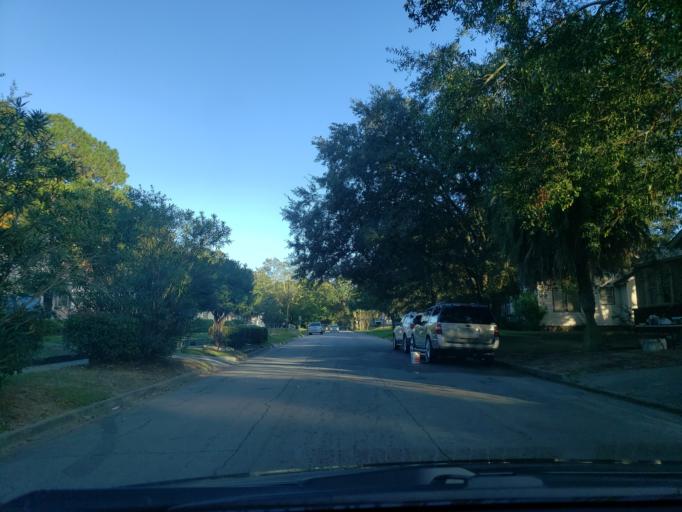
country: US
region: Georgia
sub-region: Chatham County
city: Thunderbolt
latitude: 32.0523
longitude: -81.0774
